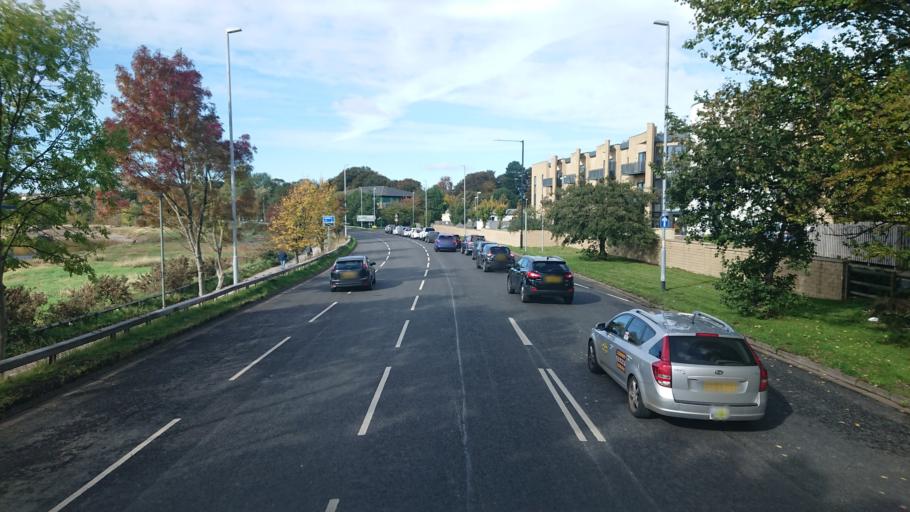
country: GB
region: England
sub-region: Lancashire
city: Lancaster
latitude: 54.0538
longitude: -2.8026
